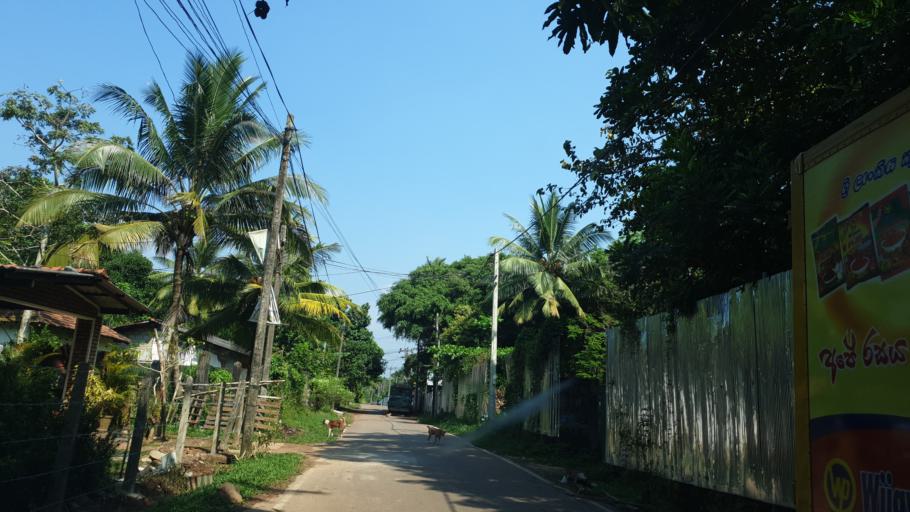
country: LK
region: Western
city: Moratuwa
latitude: 6.7599
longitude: 79.9234
